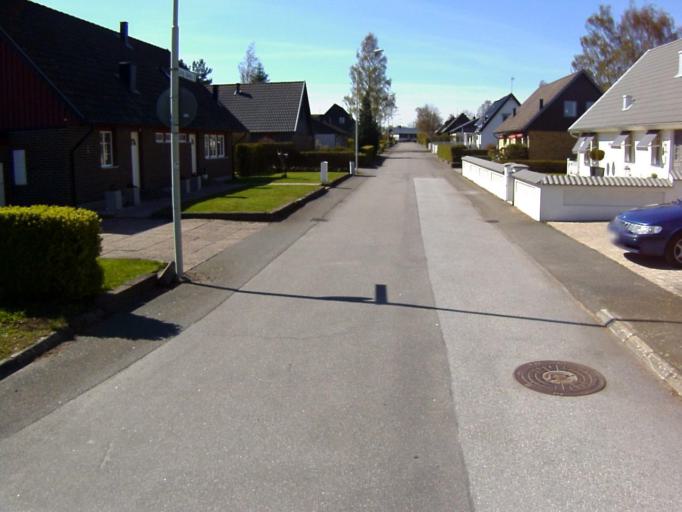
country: SE
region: Skane
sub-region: Kristianstads Kommun
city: Norra Asum
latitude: 55.9983
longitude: 14.0916
